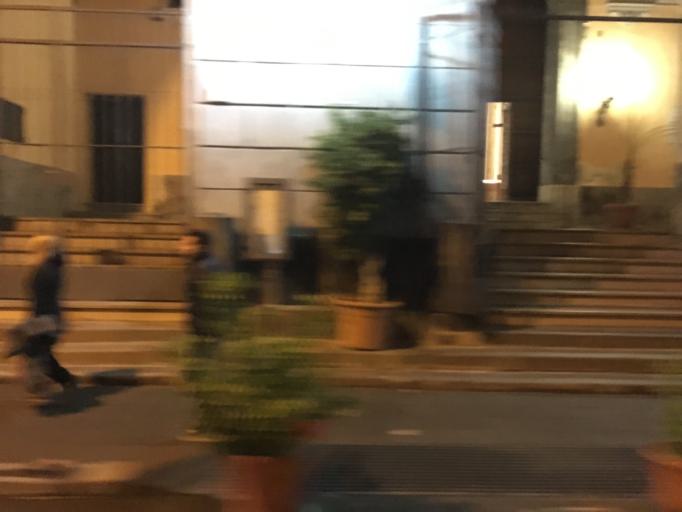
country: IT
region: Campania
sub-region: Provincia di Napoli
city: Napoli
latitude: 40.8331
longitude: 14.2284
